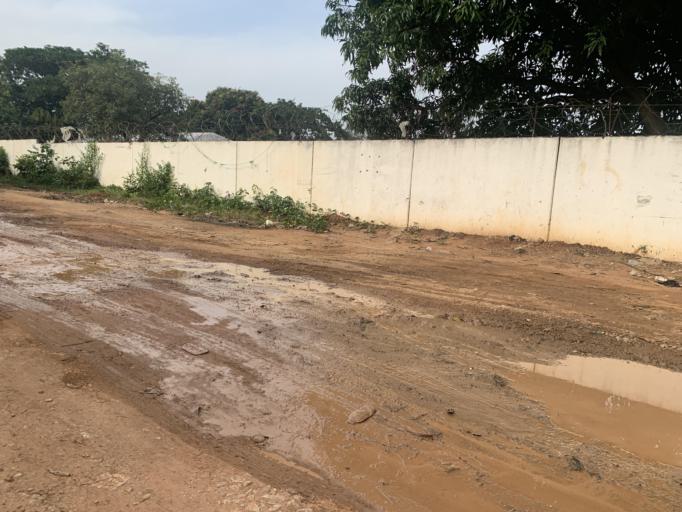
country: NG
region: Abuja Federal Capital Territory
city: Abuja
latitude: 9.0334
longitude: 7.3965
